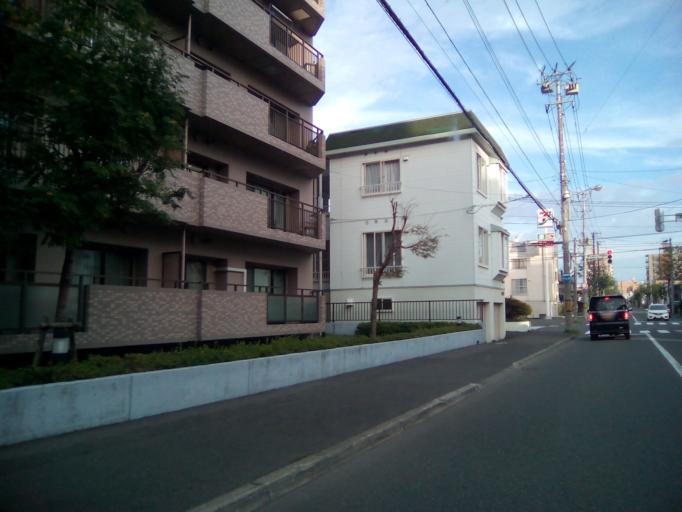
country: JP
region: Hokkaido
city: Sapporo
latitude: 43.0551
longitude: 141.3861
